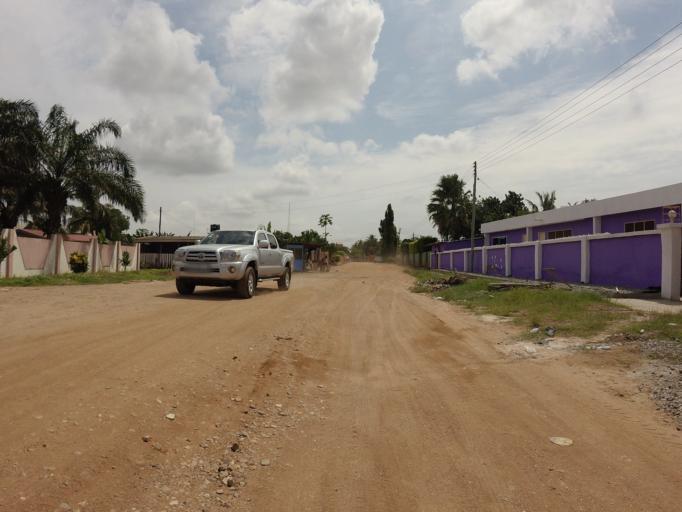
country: GH
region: Greater Accra
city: Dome
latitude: 5.6379
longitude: -0.2356
